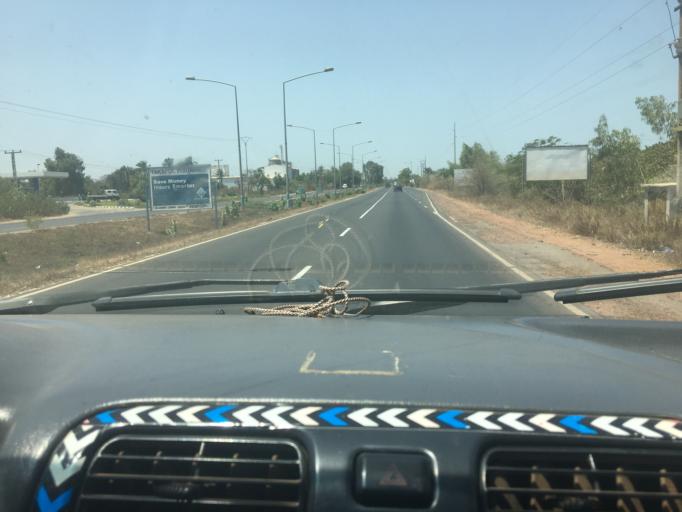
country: GM
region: Banjul
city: Bakau
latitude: 13.4672
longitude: -16.6490
